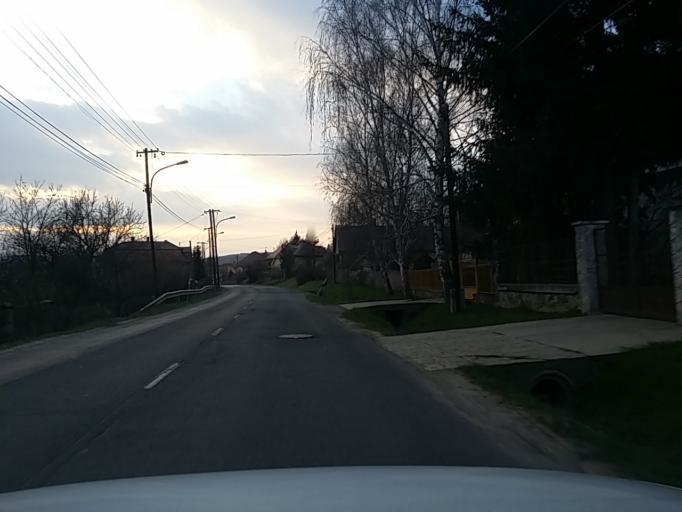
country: HU
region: Nograd
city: Matraterenye
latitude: 48.0053
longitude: 19.9060
